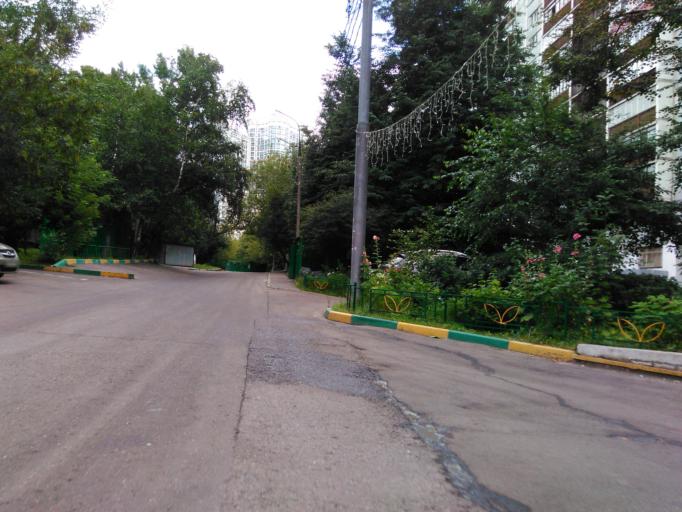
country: RU
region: Moscow
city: Troparevo
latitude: 55.6656
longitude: 37.5079
